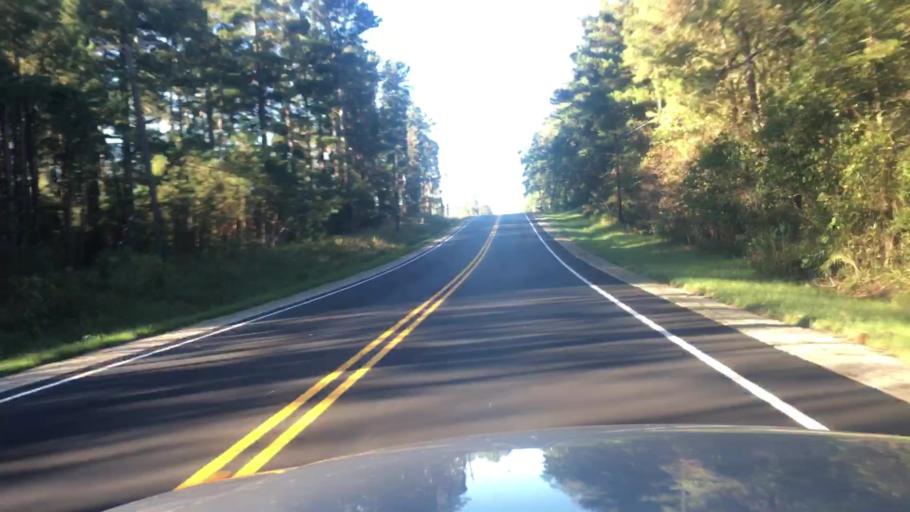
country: US
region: North Carolina
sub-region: Harnett County
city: Walkertown
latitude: 35.3208
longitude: -78.8735
